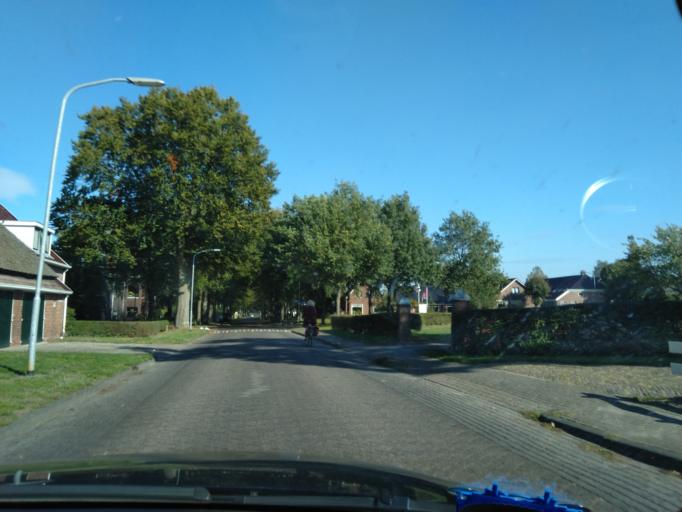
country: NL
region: Drenthe
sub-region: Gemeente Aa en Hunze
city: Anloo
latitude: 53.0547
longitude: 6.7308
